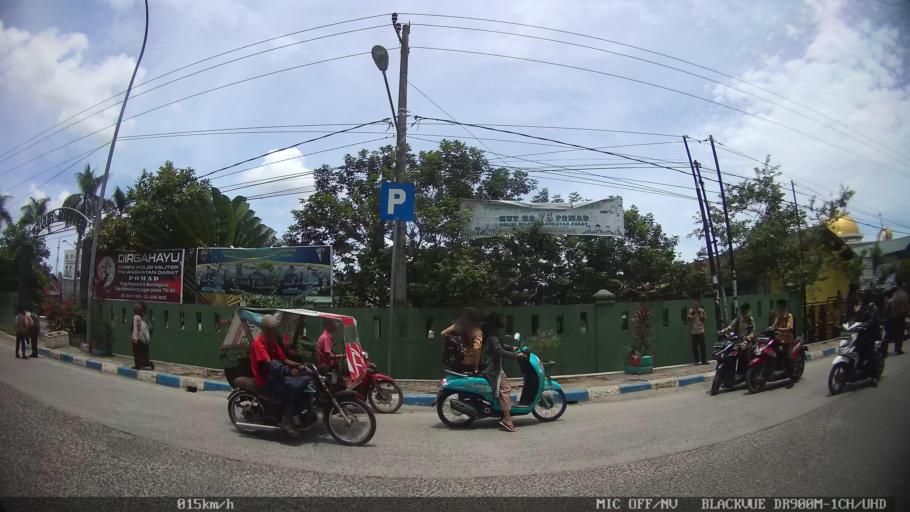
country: ID
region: North Sumatra
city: Percut
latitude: 3.5585
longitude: 98.8799
